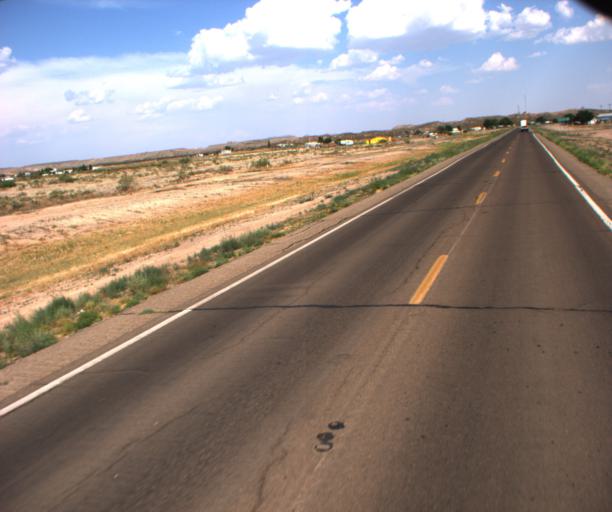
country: US
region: Arizona
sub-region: Greenlee County
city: Clifton
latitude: 32.7434
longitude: -109.1007
